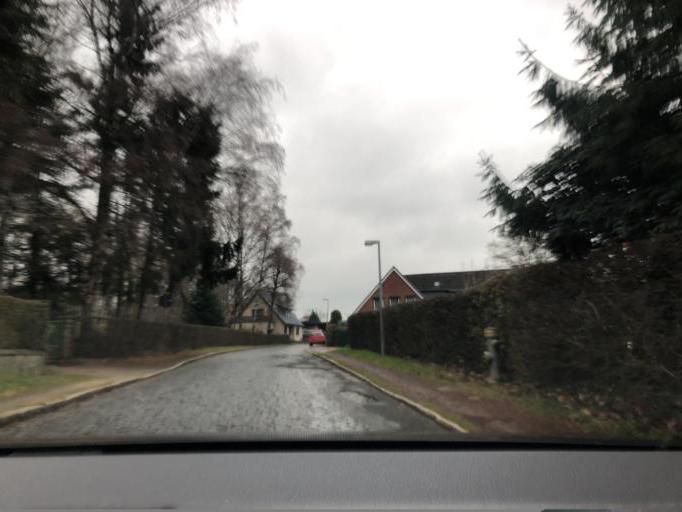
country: DE
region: Lower Saxony
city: Ritterhude
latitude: 53.1743
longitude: 8.7364
